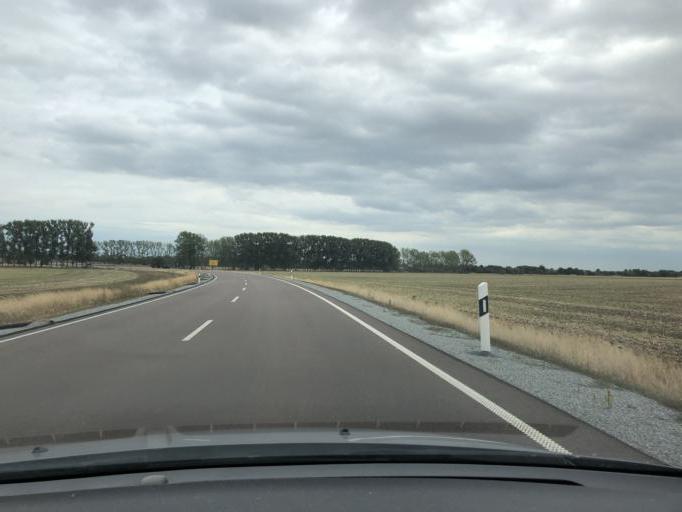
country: DE
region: Saxony-Anhalt
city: Brumby
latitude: 51.8893
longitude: 11.7074
